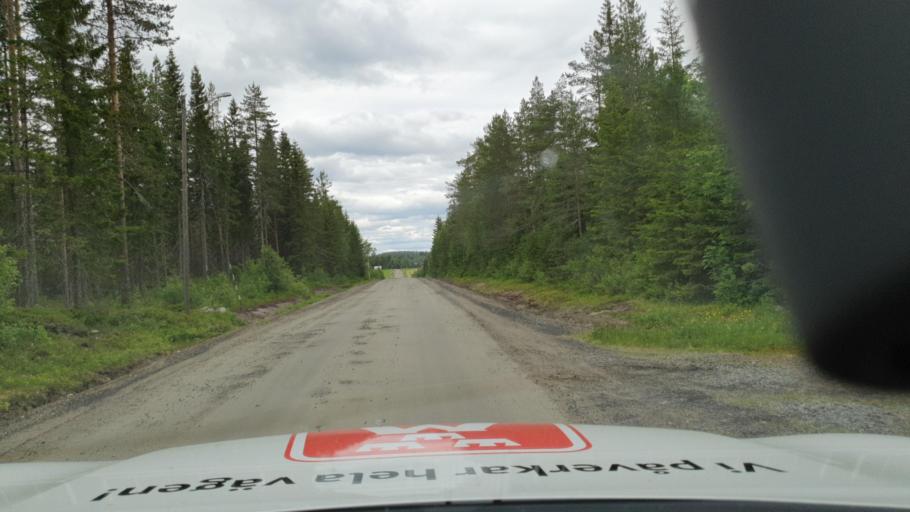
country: SE
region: Vaesterbotten
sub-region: Nordmalings Kommun
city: Nordmaling
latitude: 63.6951
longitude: 19.4435
